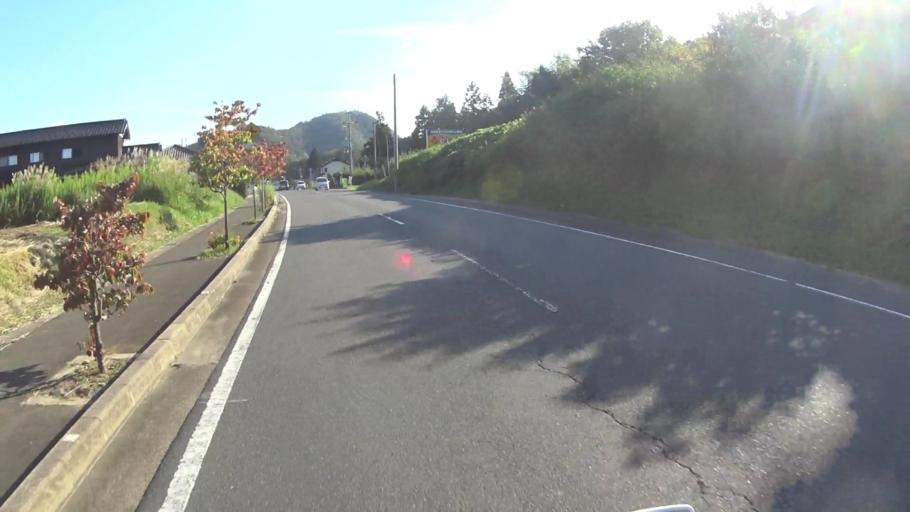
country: JP
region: Hyogo
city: Toyooka
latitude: 35.6149
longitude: 134.9194
